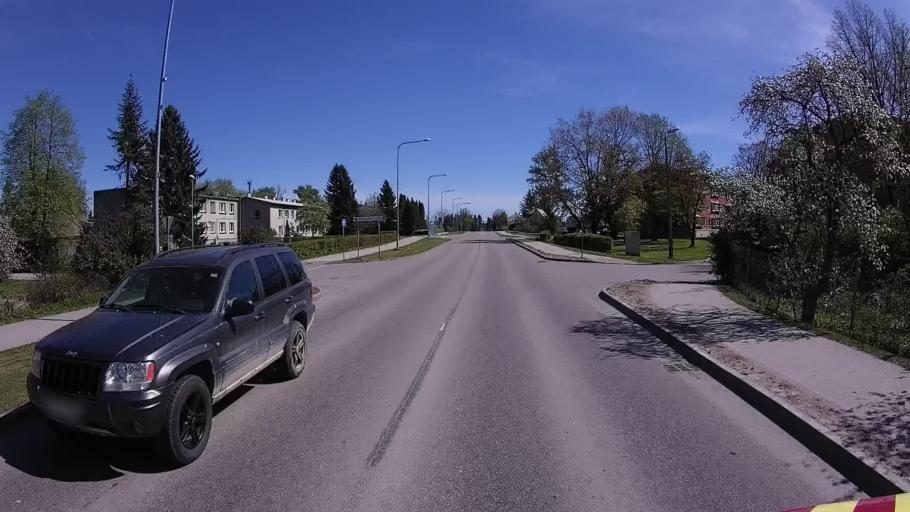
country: EE
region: Polvamaa
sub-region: Polva linn
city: Polva
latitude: 58.0697
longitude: 27.0801
